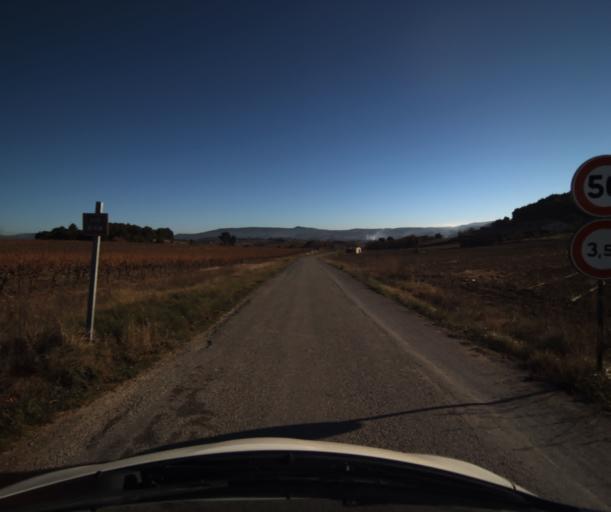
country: FR
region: Provence-Alpes-Cote d'Azur
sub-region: Departement du Vaucluse
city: Pertuis
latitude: 43.7274
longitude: 5.5091
